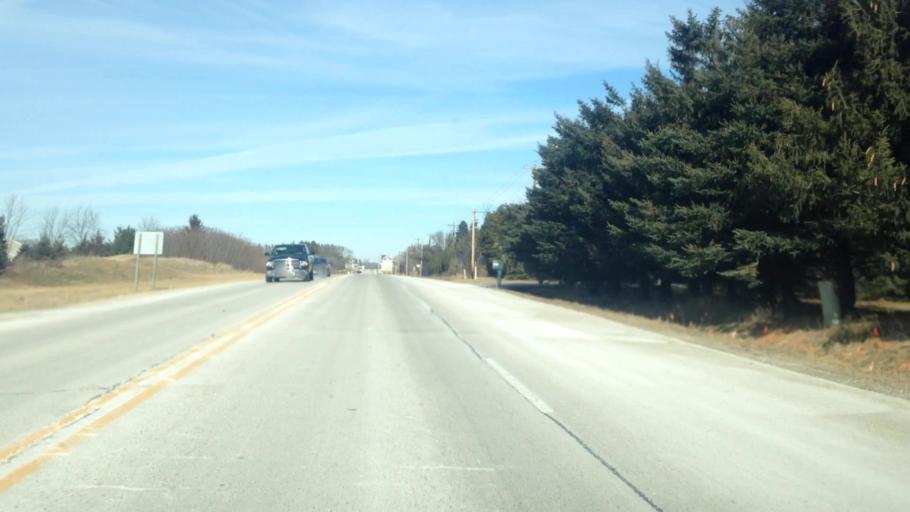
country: US
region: Wisconsin
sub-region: Washington County
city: Richfield
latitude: 43.2595
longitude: -88.2616
